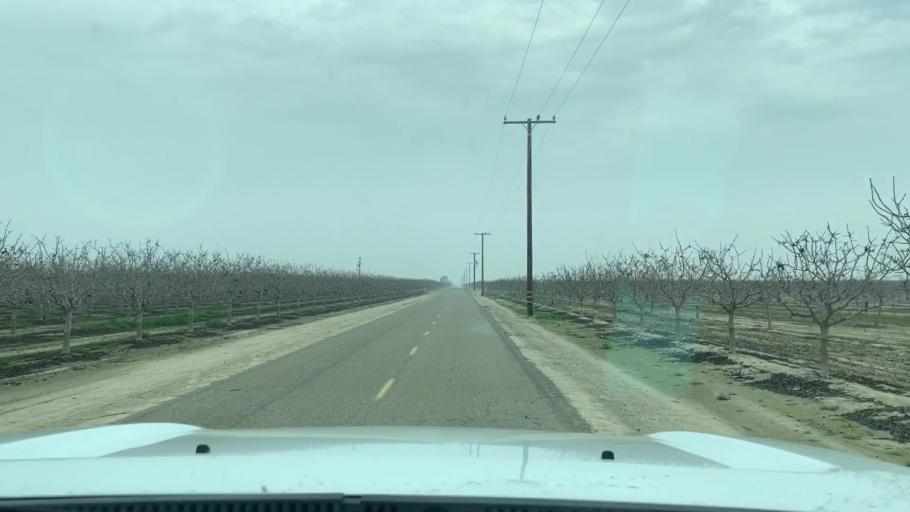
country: US
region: California
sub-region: Tulare County
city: Earlimart
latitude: 35.8193
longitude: -119.3422
